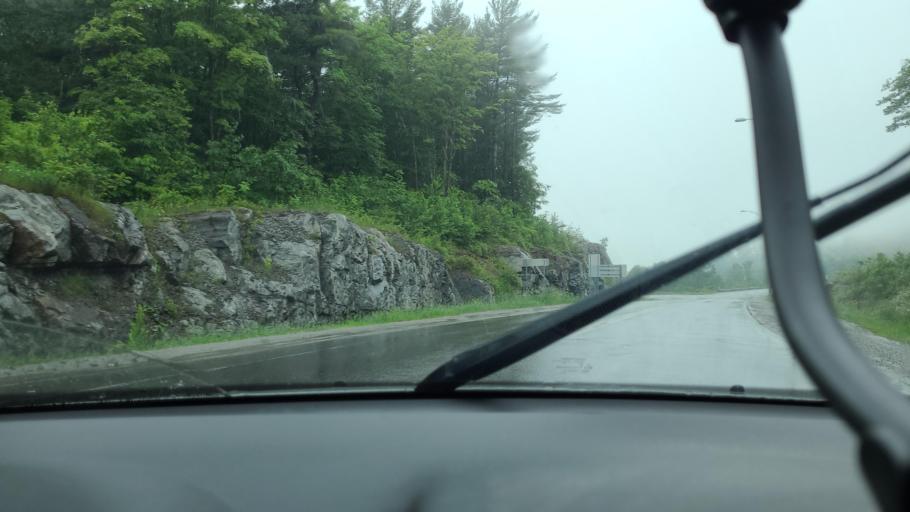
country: CA
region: Quebec
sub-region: Outaouais
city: Papineauville
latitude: 45.6609
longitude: -75.0188
